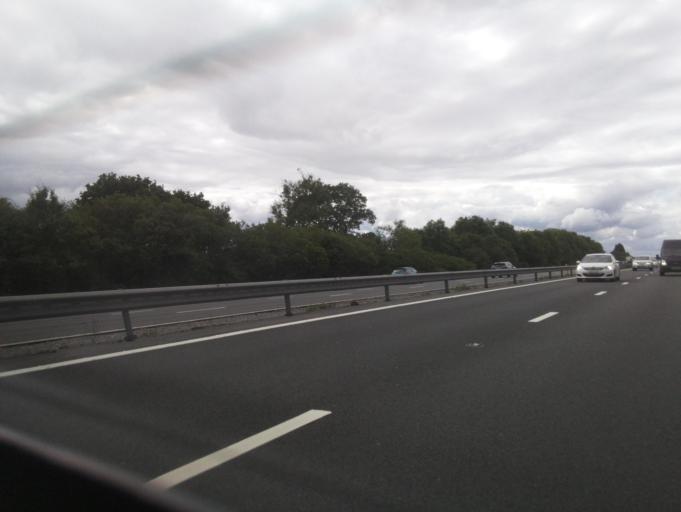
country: GB
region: England
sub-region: Wiltshire
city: Lyneham
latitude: 51.5371
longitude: -1.9962
